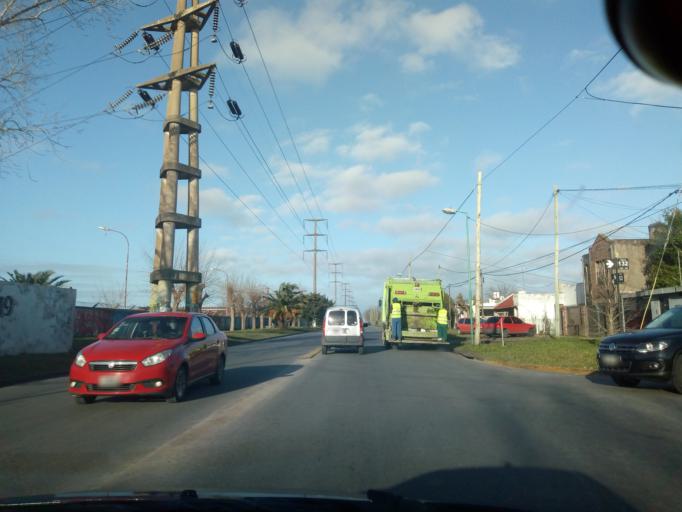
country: AR
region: Buenos Aires
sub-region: Partido de La Plata
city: La Plata
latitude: -34.9395
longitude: -57.9744
